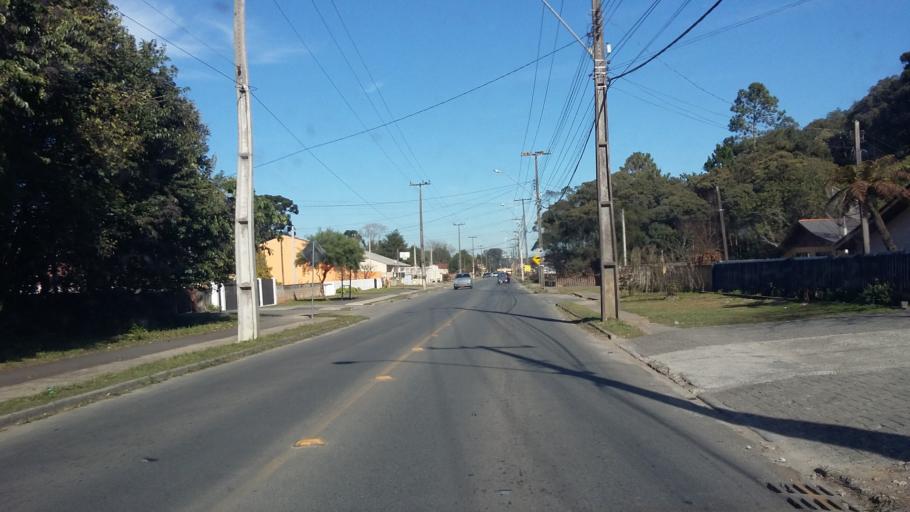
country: BR
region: Parana
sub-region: Campo Largo
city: Campo Largo
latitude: -25.4643
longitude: -49.5616
